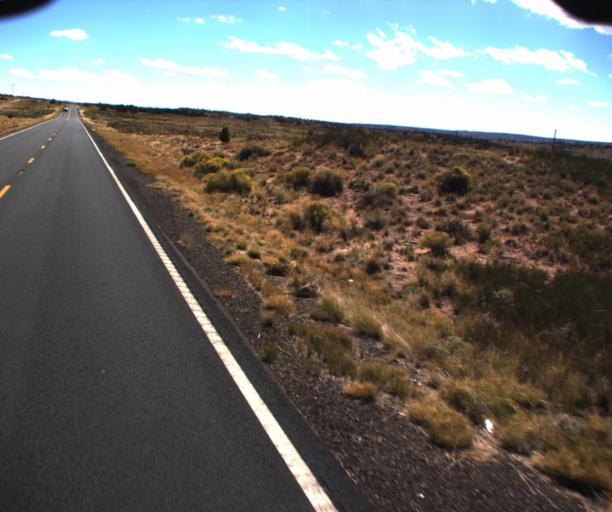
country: US
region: Arizona
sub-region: Apache County
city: Houck
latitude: 35.0802
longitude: -109.3024
